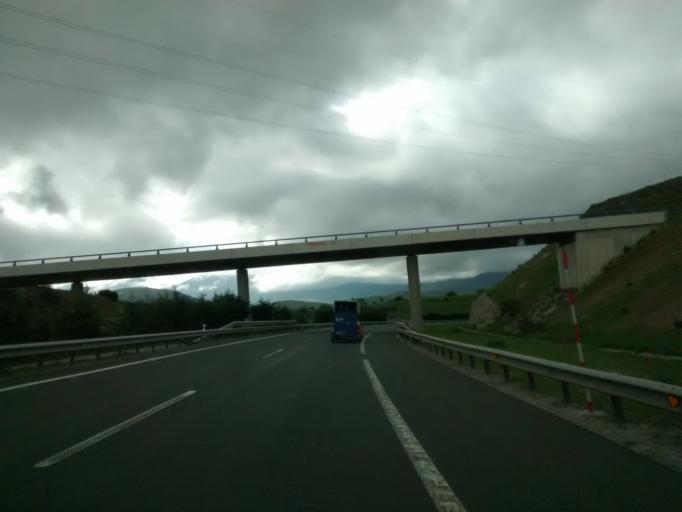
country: ES
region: Cantabria
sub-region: Provincia de Cantabria
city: Villaescusa
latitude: 42.9558
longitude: -4.1545
